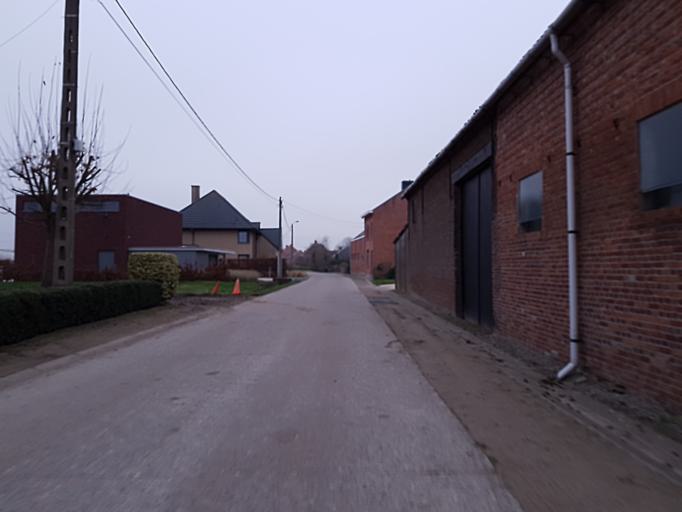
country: BE
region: Flanders
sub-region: Provincie Vlaams-Brabant
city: Kapelle-op-den-Bos
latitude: 51.0244
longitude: 4.4055
